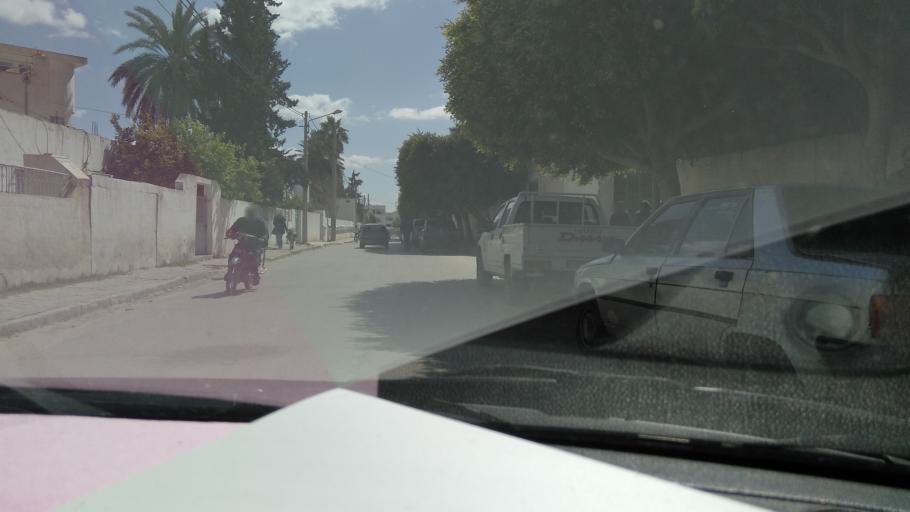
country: TN
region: Al Qayrawan
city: Kairouan
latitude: 35.6705
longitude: 10.1062
